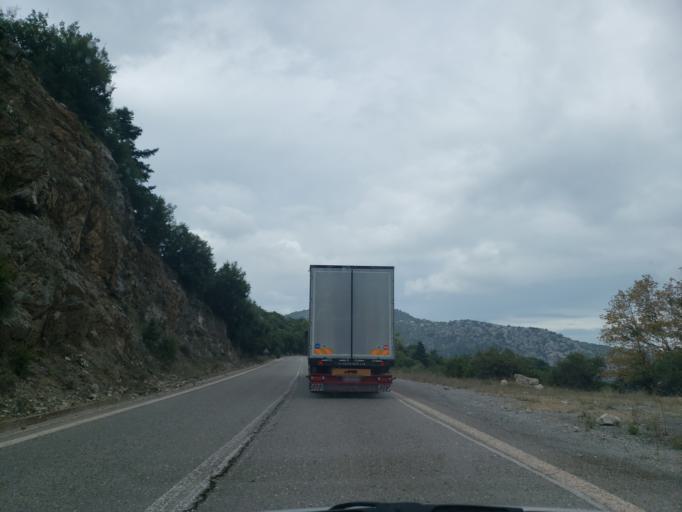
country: GR
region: Central Greece
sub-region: Nomos Fokidos
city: Amfissa
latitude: 38.6419
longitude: 22.3963
